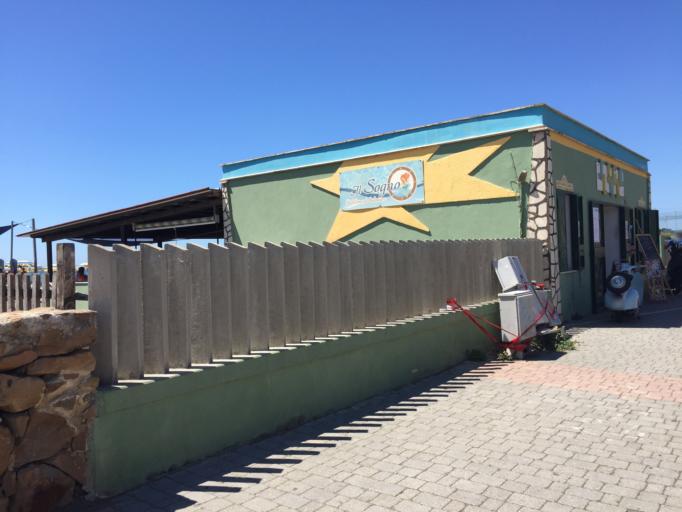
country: IT
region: Latium
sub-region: Citta metropolitana di Roma Capitale
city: Ladispoli
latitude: 41.9503
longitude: 12.0707
